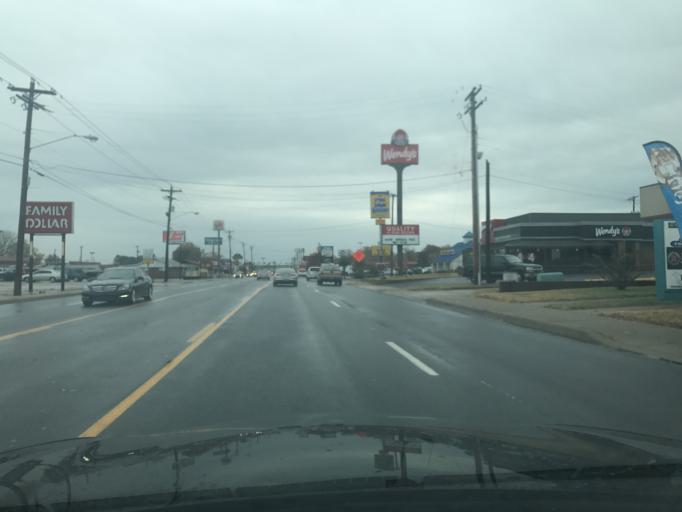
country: US
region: Arkansas
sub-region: Faulkner County
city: Conway
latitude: 35.0916
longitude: -92.4308
